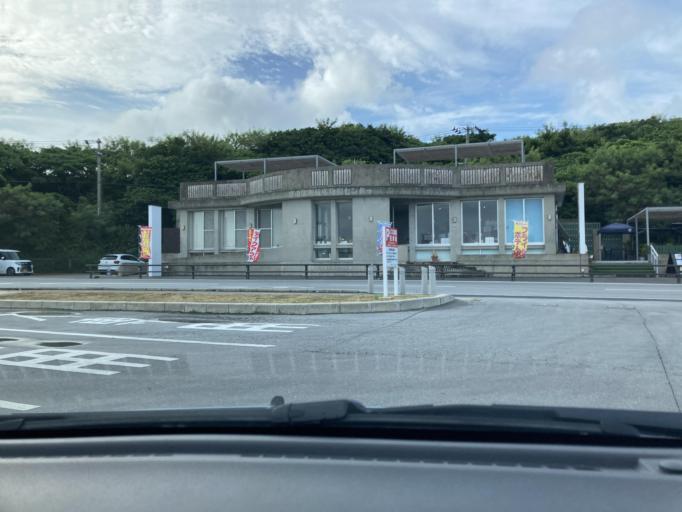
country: JP
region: Okinawa
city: Tomigusuku
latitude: 26.1753
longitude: 127.6442
